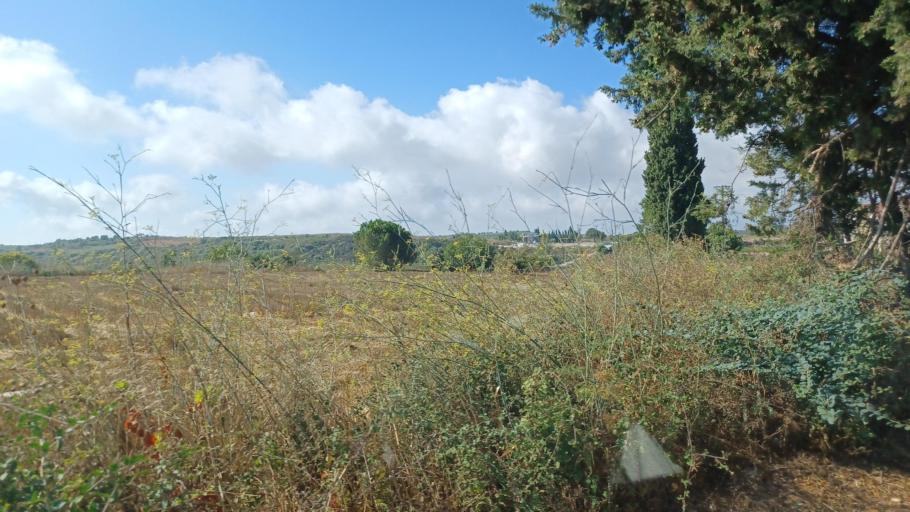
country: CY
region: Pafos
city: Pegeia
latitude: 34.9068
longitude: 32.4229
